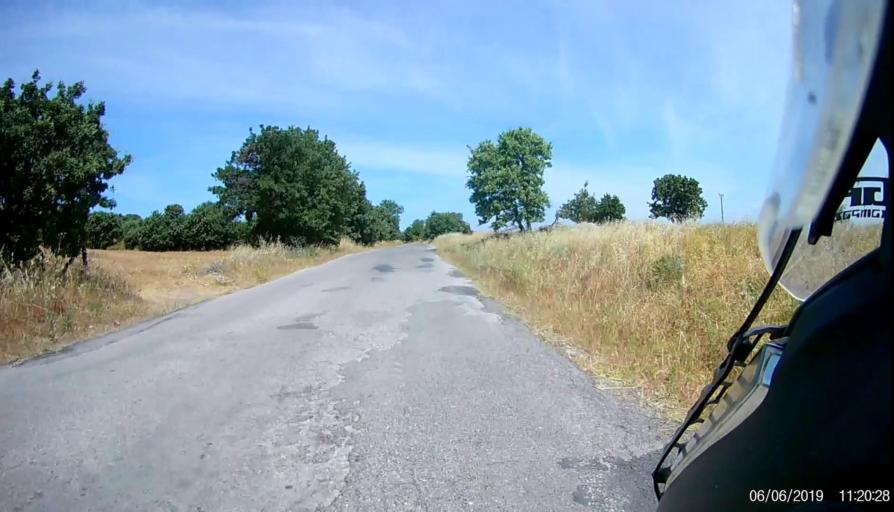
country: TR
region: Canakkale
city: Gulpinar
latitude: 39.6667
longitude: 26.1635
